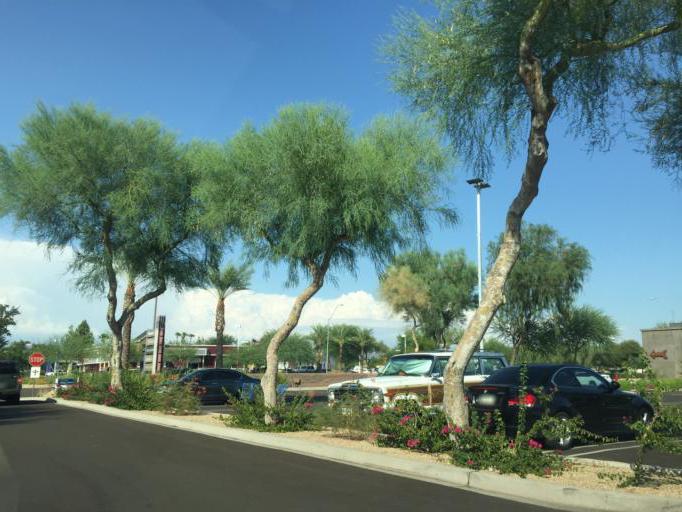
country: US
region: Arizona
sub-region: Maricopa County
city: Paradise Valley
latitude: 33.5974
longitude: -111.9784
